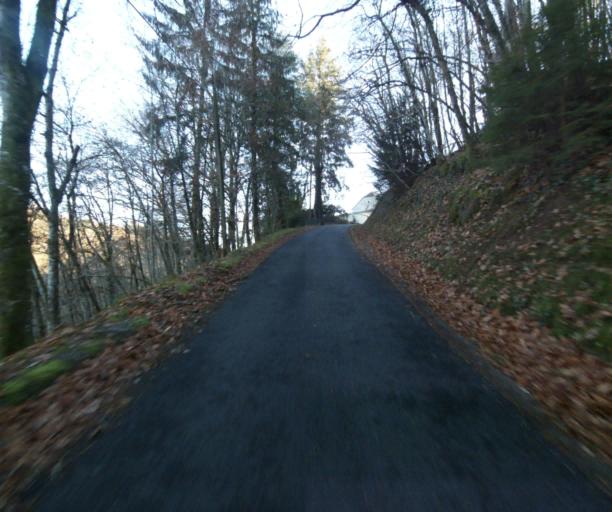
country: FR
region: Limousin
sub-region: Departement de la Correze
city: Laguenne
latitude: 45.2350
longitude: 1.8013
